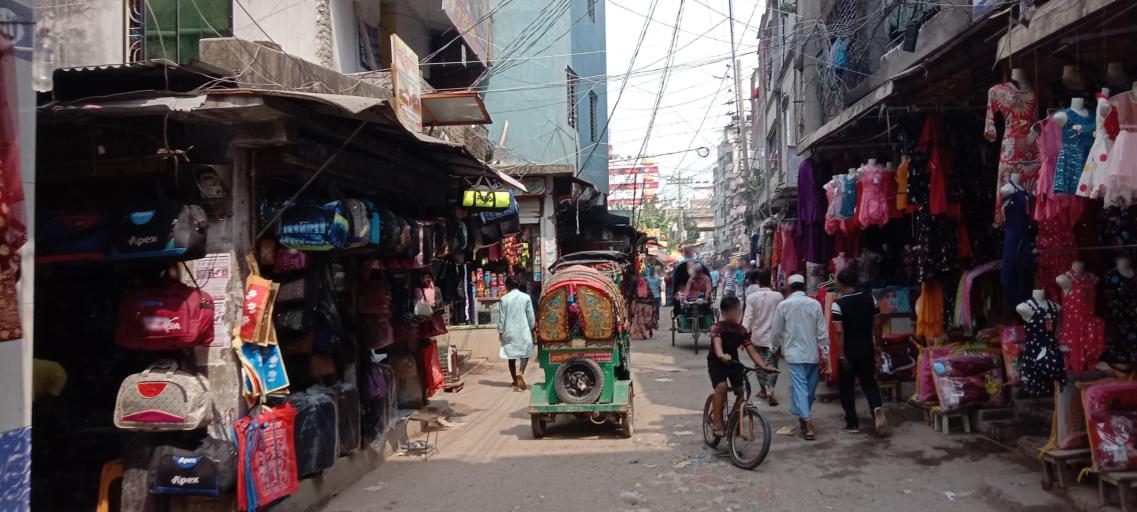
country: BD
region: Dhaka
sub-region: Dhaka
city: Dhaka
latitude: 23.7073
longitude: 90.3989
